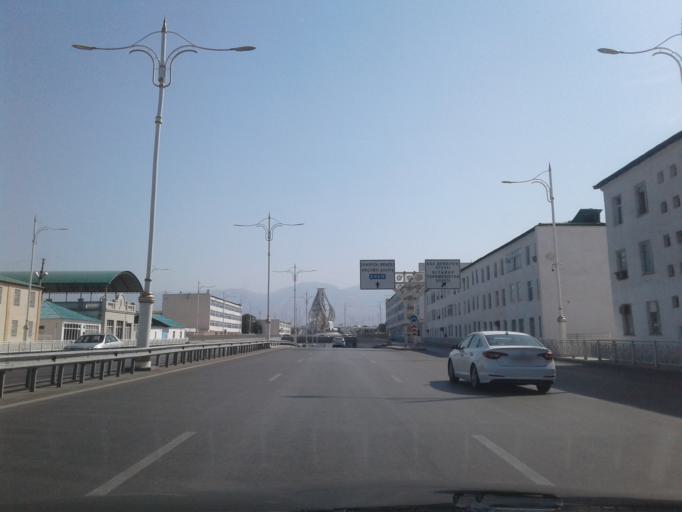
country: TM
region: Ahal
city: Ashgabat
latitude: 37.9460
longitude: 58.4055
